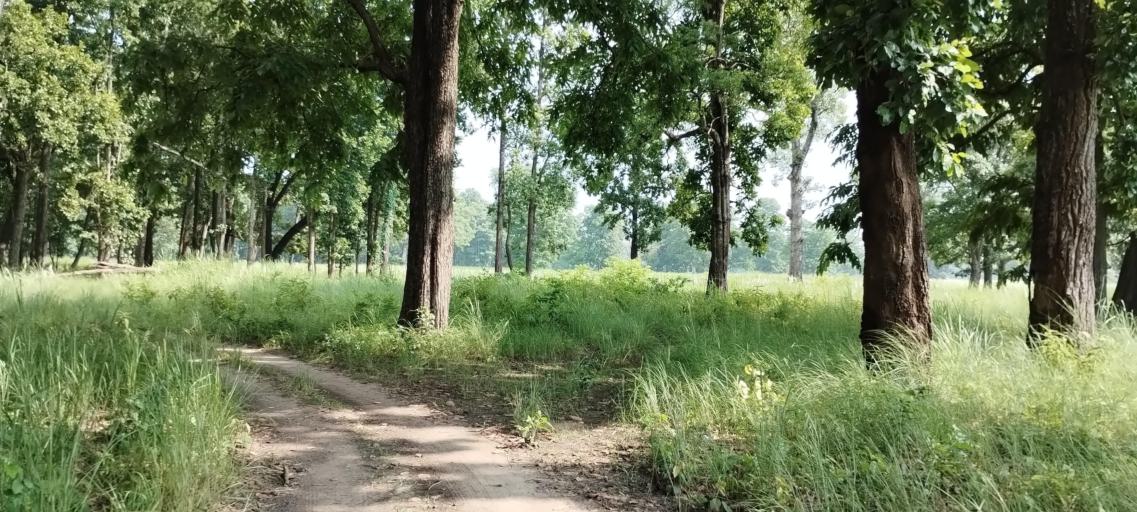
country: NP
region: Far Western
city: Tikapur
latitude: 28.5067
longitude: 81.2506
